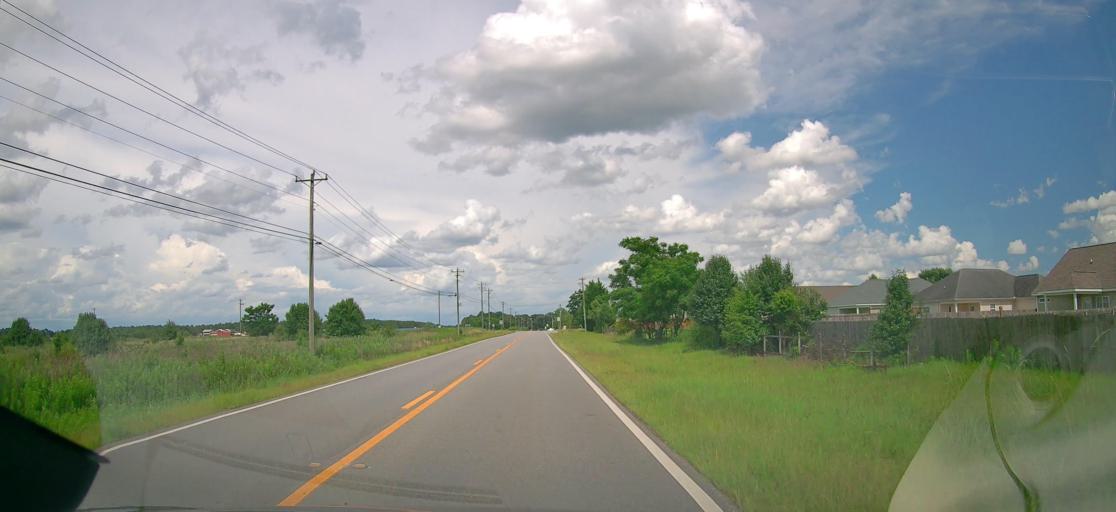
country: US
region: Georgia
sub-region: Houston County
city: Centerville
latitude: 32.5785
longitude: -83.7025
